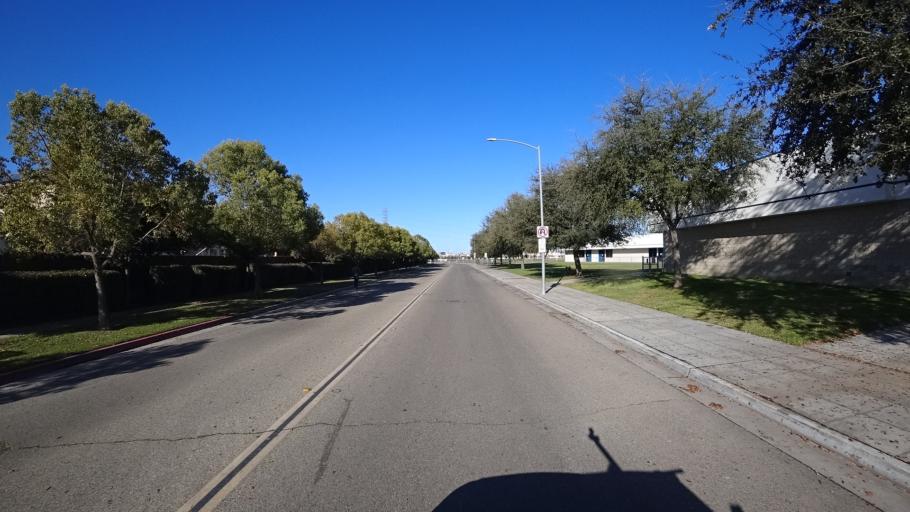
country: US
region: California
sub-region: Fresno County
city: Biola
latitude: 36.8334
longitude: -119.9052
